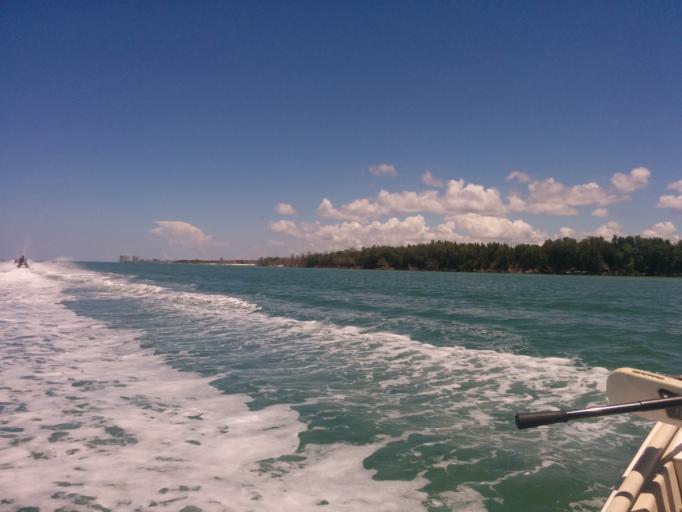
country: US
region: Florida
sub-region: Collier County
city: Marco
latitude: 25.8463
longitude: -81.6832
